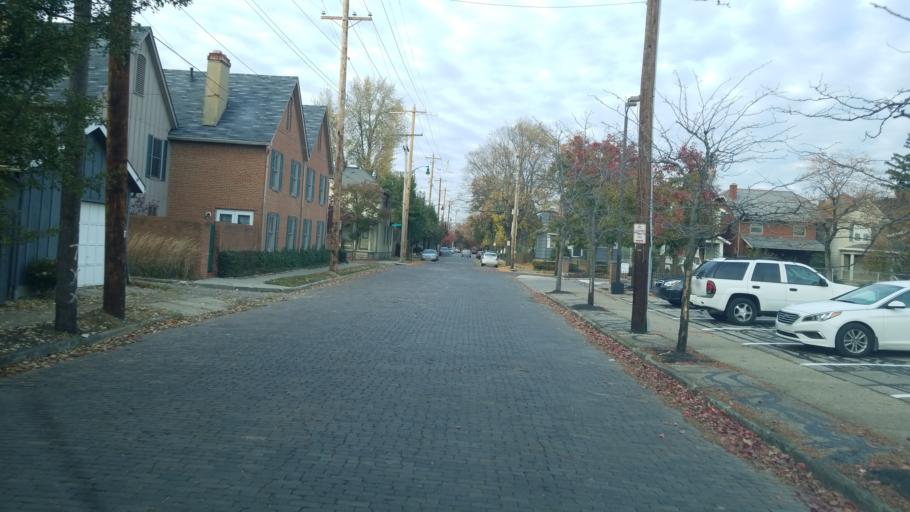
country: US
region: Ohio
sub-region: Franklin County
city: Columbus
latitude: 39.9454
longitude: -82.9900
